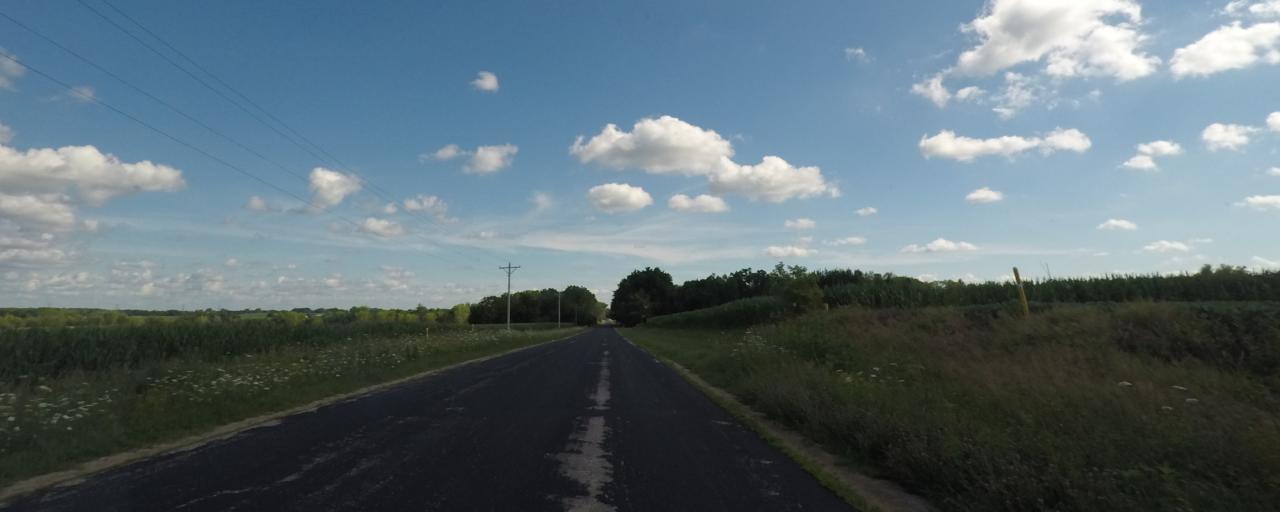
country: US
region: Wisconsin
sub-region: Rock County
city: Edgerton
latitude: 42.8565
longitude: -89.1320
